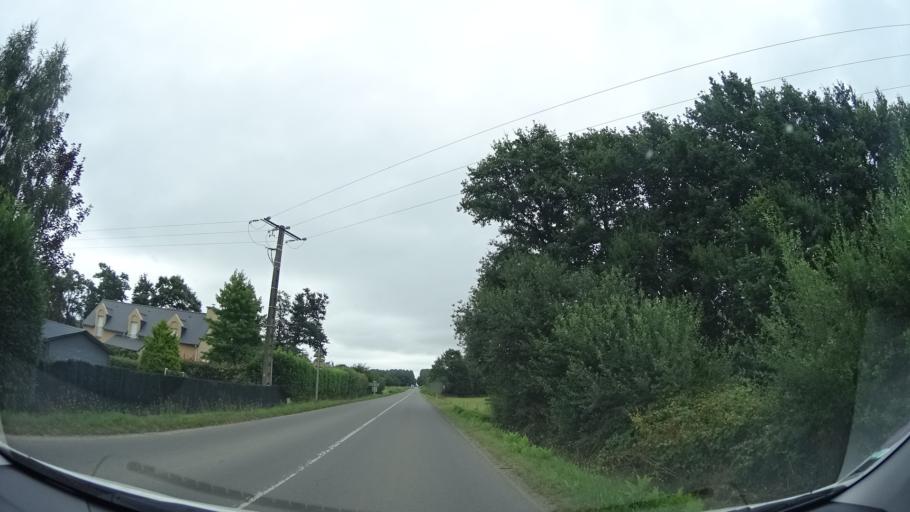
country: FR
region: Brittany
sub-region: Departement d'Ille-et-Vilaine
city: Meillac
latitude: 48.3847
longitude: -1.8208
